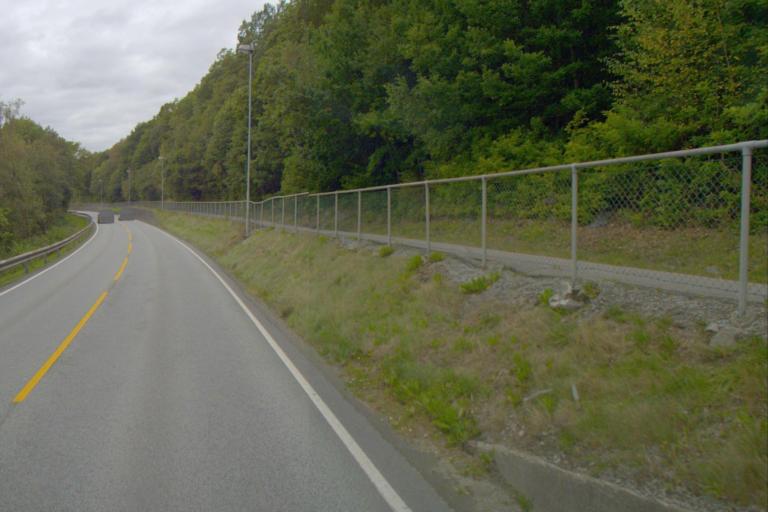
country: NO
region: Rogaland
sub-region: Sandnes
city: Sandnes
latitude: 58.8691
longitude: 5.8041
